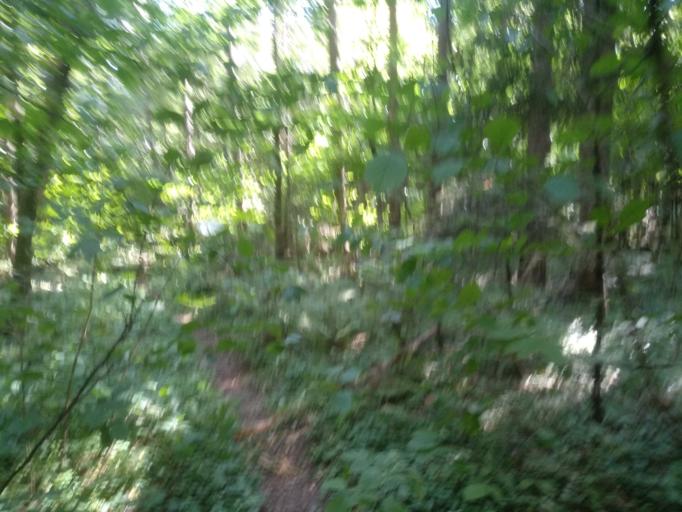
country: RU
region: Moskovskaya
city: Dedovsk
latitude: 55.8740
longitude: 37.0912
